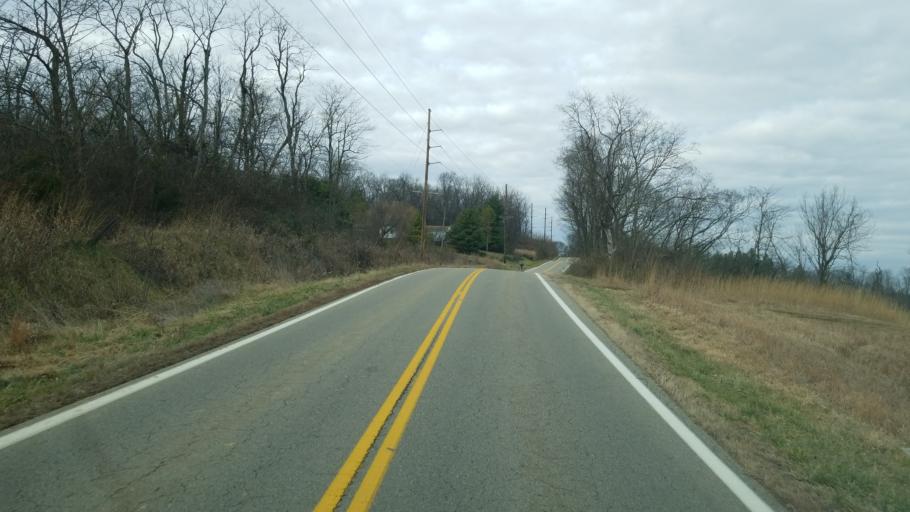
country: US
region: Ohio
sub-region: Ross County
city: Frankfort
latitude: 39.3495
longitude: -83.2200
